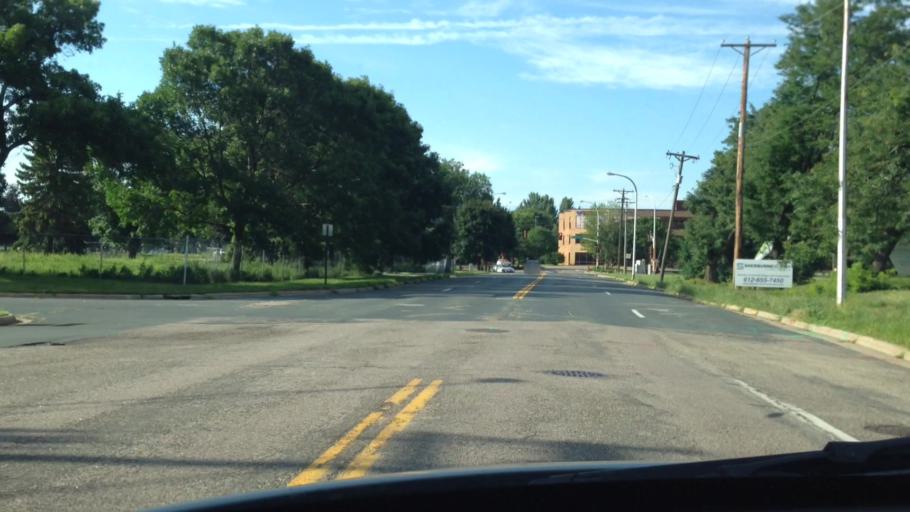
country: US
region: Minnesota
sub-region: Hennepin County
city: Edina
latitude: 44.8618
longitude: -93.3457
